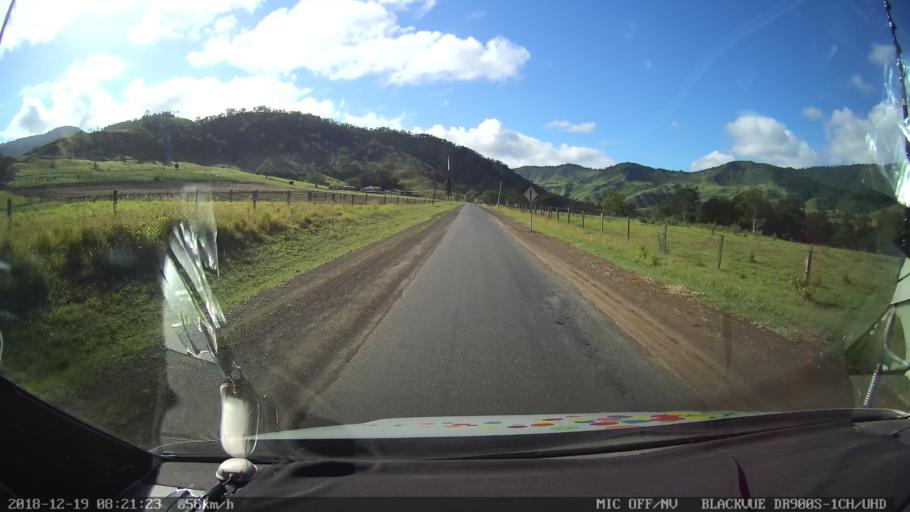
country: AU
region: New South Wales
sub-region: Kyogle
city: Kyogle
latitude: -28.2966
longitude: 152.9098
